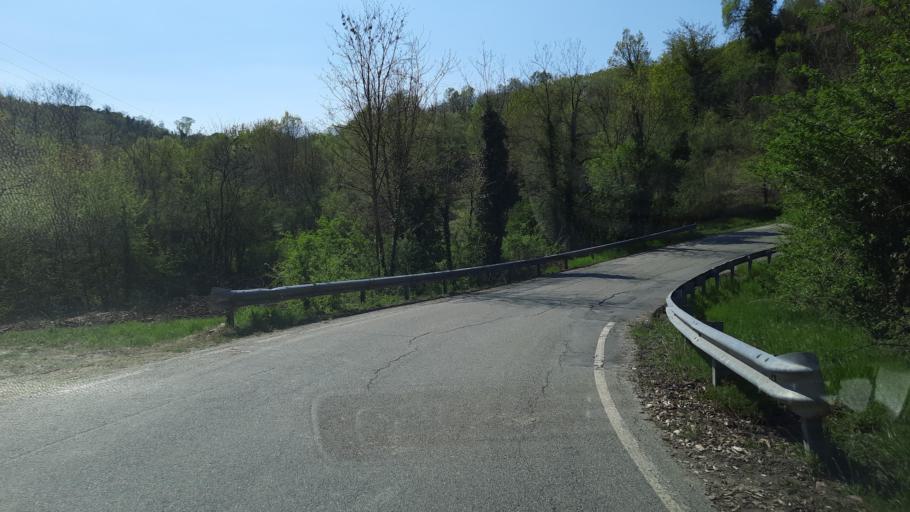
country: IT
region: Piedmont
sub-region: Provincia di Torino
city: Valentino
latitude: 45.1535
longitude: 8.1093
